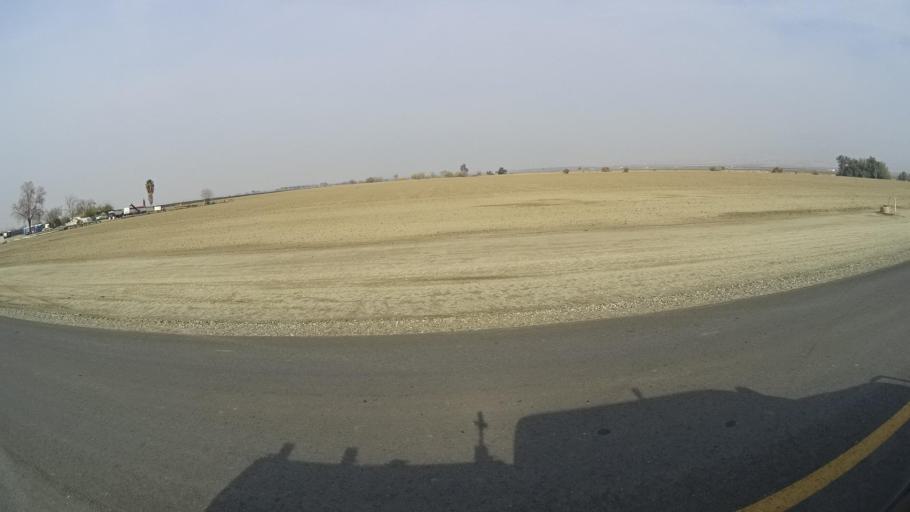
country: US
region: California
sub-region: Kern County
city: Arvin
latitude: 35.0453
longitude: -118.8623
